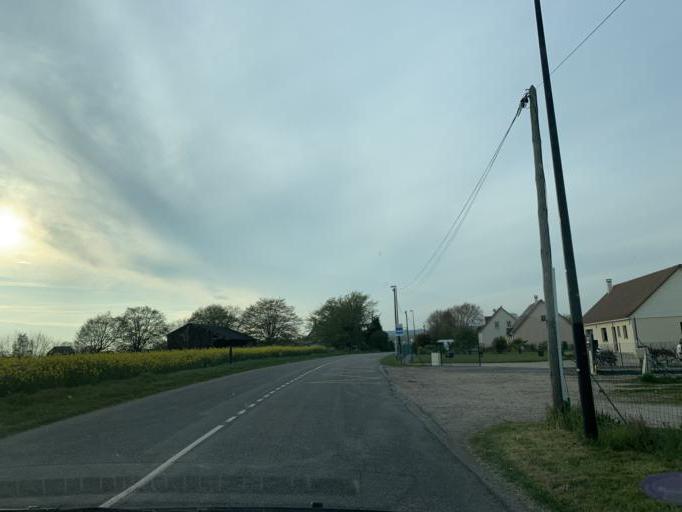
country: FR
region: Haute-Normandie
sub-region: Departement de la Seine-Maritime
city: Caudebec-en-Caux
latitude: 49.5039
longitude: 0.7441
